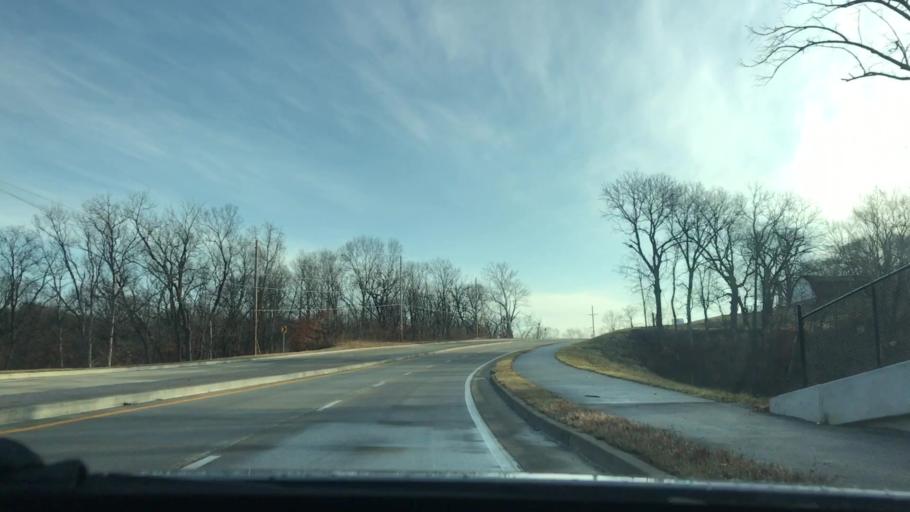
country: US
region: Missouri
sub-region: Platte County
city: Weatherby Lake
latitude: 39.2251
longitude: -94.7526
